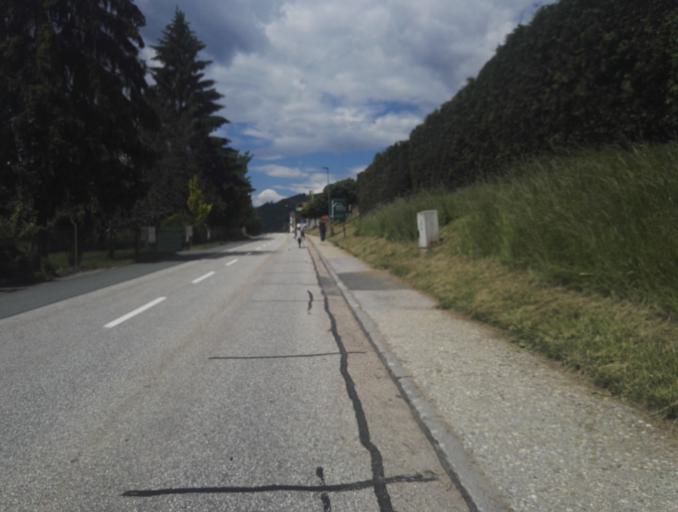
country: AT
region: Styria
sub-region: Politischer Bezirk Graz-Umgebung
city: Ubelbach
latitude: 47.2230
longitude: 15.2441
